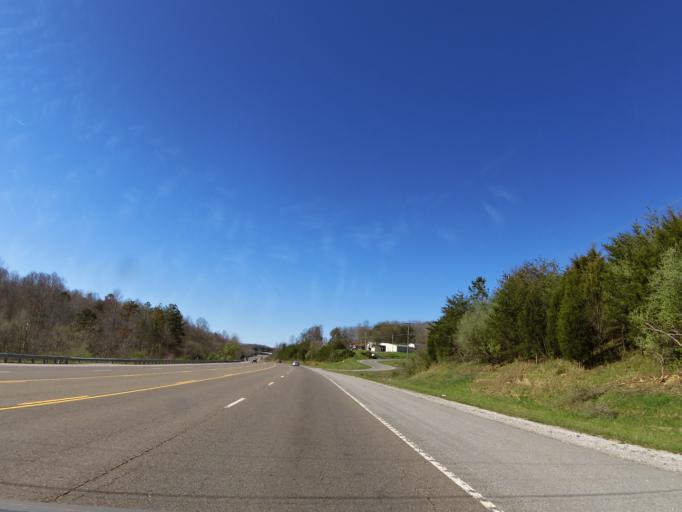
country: US
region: Tennessee
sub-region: Scott County
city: Oneida
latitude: 36.4465
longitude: -84.5412
